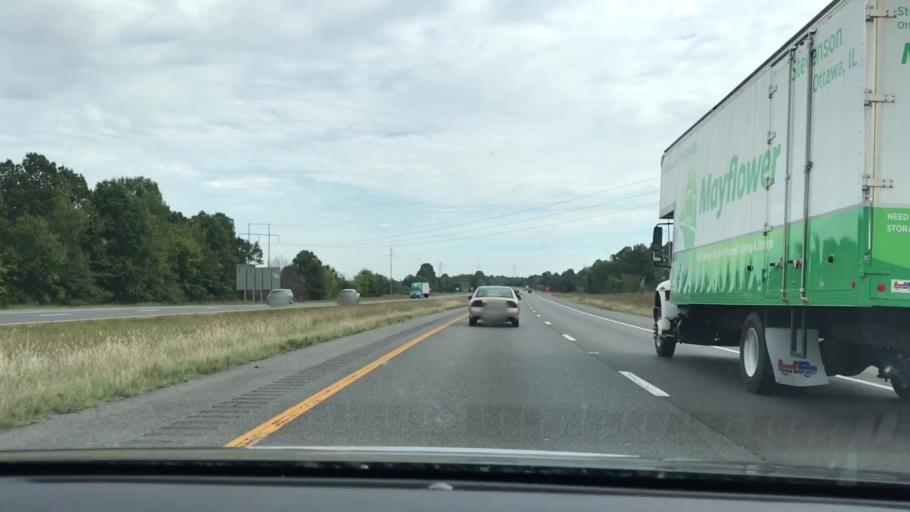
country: US
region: Kentucky
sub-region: Marshall County
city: Calvert City
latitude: 37.0143
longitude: -88.3088
